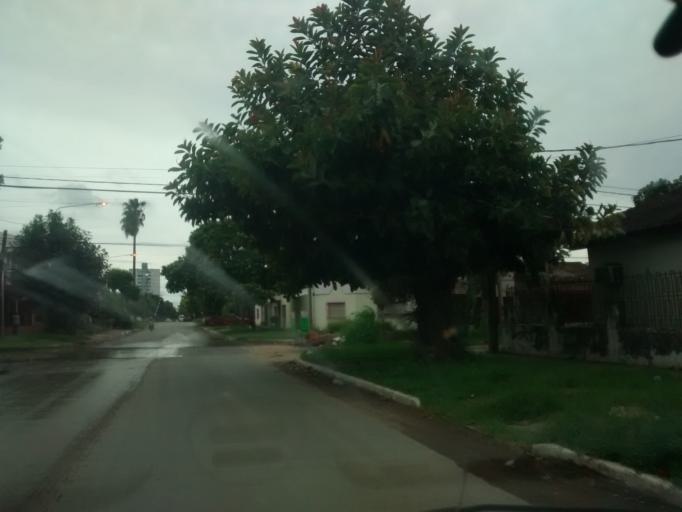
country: AR
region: Chaco
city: Resistencia
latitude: -27.4474
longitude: -59.0019
